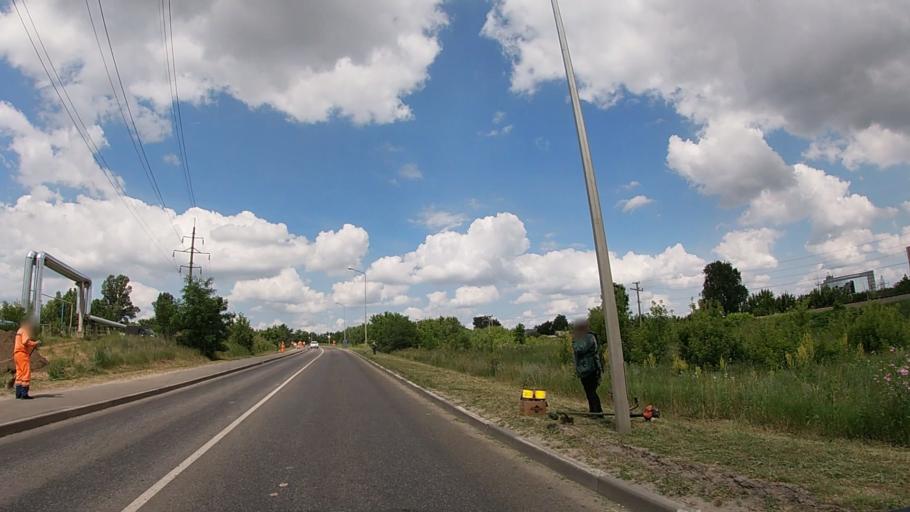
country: RU
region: Belgorod
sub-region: Belgorodskiy Rayon
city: Belgorod
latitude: 50.5928
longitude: 36.5608
